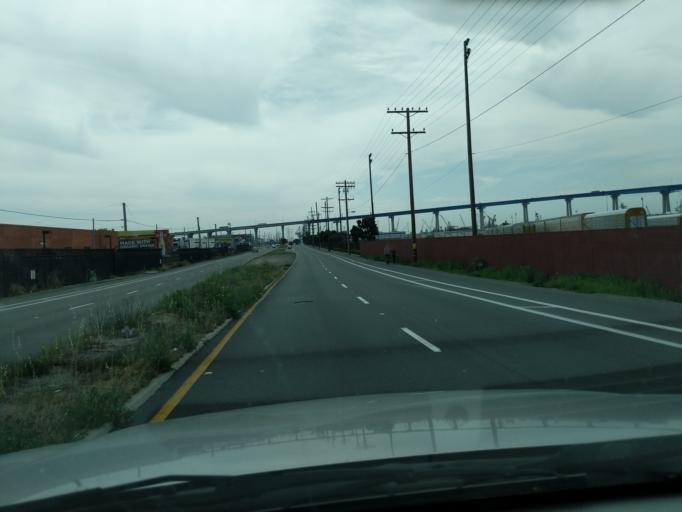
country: US
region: California
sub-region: San Diego County
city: San Diego
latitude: 32.7020
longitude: -117.1531
